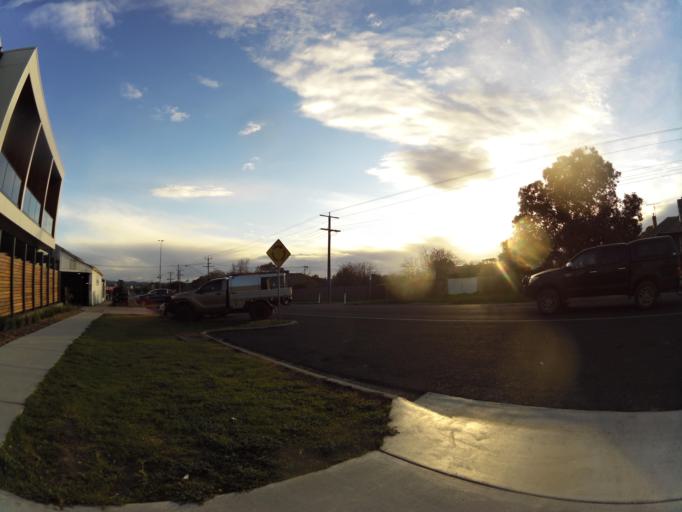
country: AU
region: Victoria
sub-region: Bass Coast
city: North Wonthaggi
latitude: -38.6067
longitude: 145.5936
